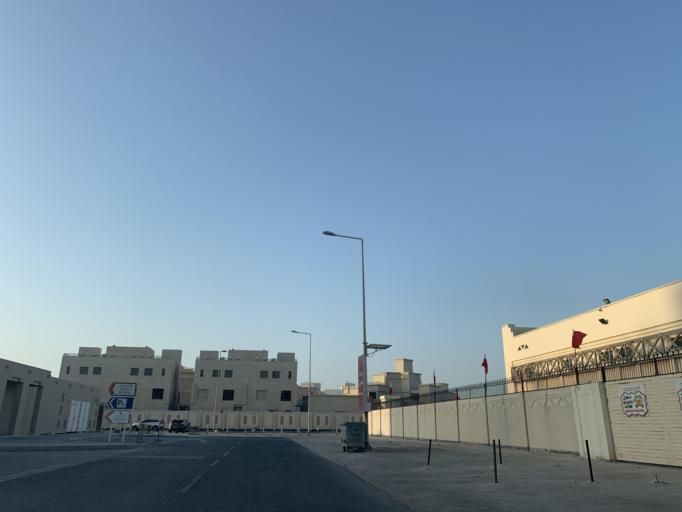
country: BH
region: Muharraq
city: Al Muharraq
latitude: 26.2660
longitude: 50.5999
